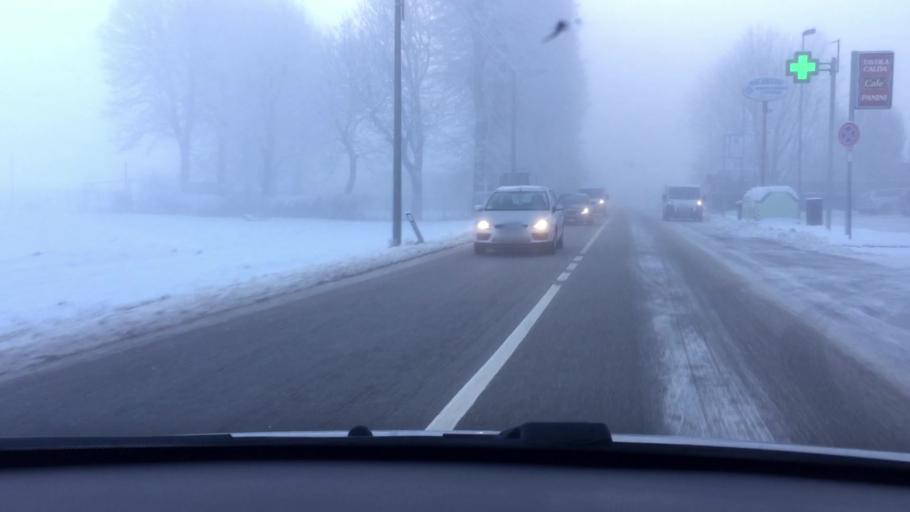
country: IT
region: Piedmont
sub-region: Provincia di Torino
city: Scalenghe
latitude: 44.8928
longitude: 7.4919
